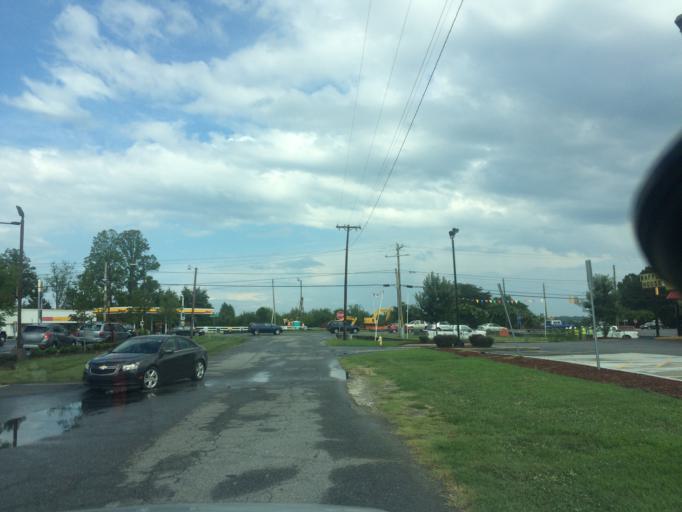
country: US
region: North Carolina
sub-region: Catawba County
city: Conover
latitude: 35.7048
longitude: -81.2638
